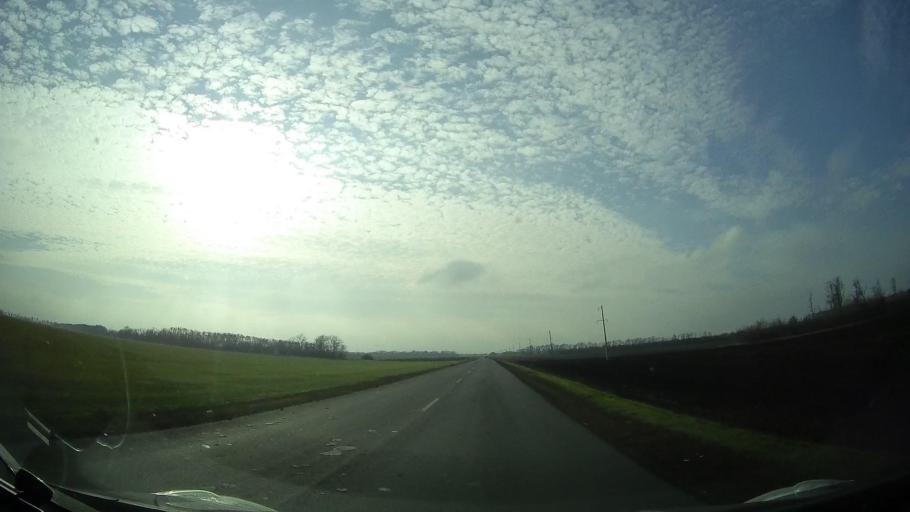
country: RU
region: Rostov
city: Mechetinskaya
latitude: 46.8052
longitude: 40.5246
